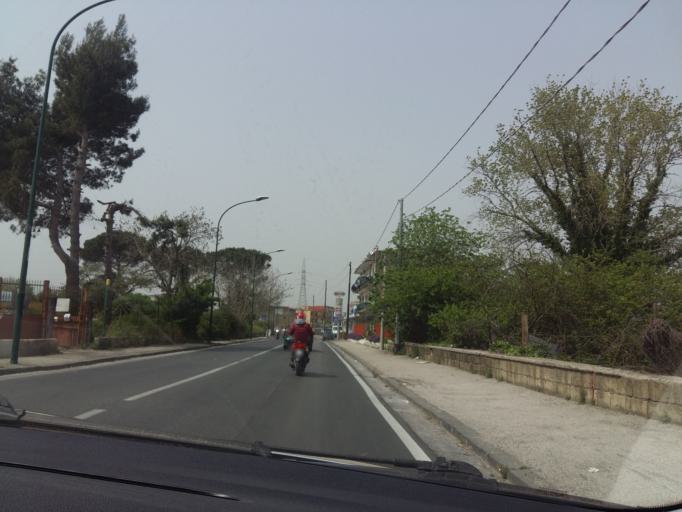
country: IT
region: Campania
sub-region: Provincia di Napoli
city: Mugnano di Napoli
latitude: 40.8969
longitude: 14.2124
